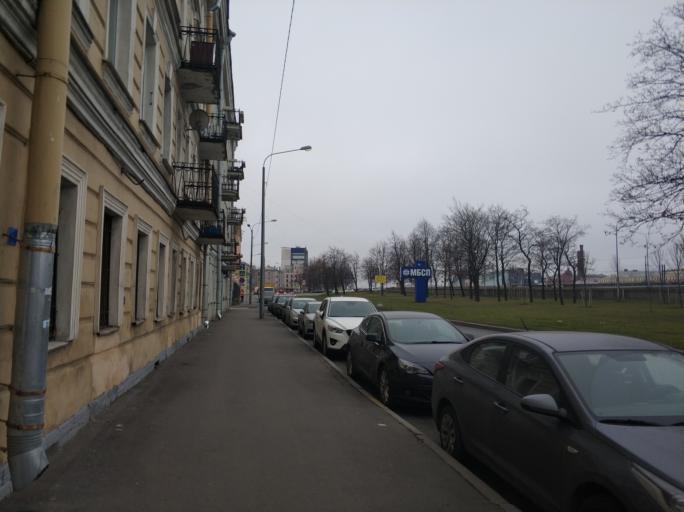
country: RU
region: Leningrad
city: Sampsonievskiy
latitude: 59.9700
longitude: 30.3368
